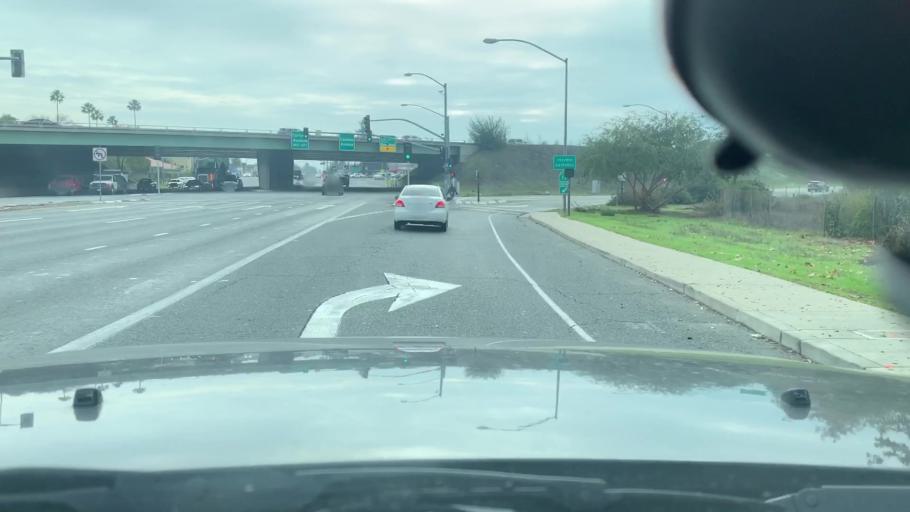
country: US
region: California
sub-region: Santa Clara County
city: Campbell
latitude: 37.2716
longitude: -121.9484
